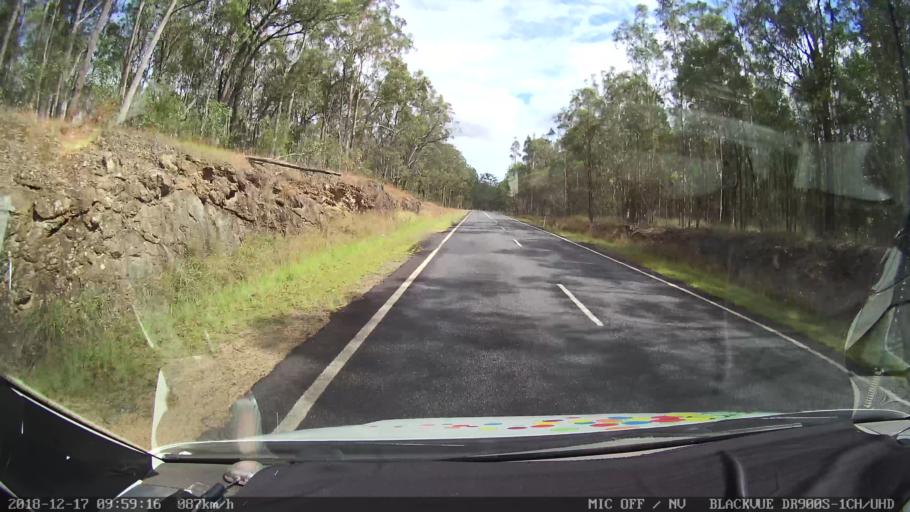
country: AU
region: New South Wales
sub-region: Tenterfield Municipality
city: Carrolls Creek
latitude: -28.9121
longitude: 152.4145
